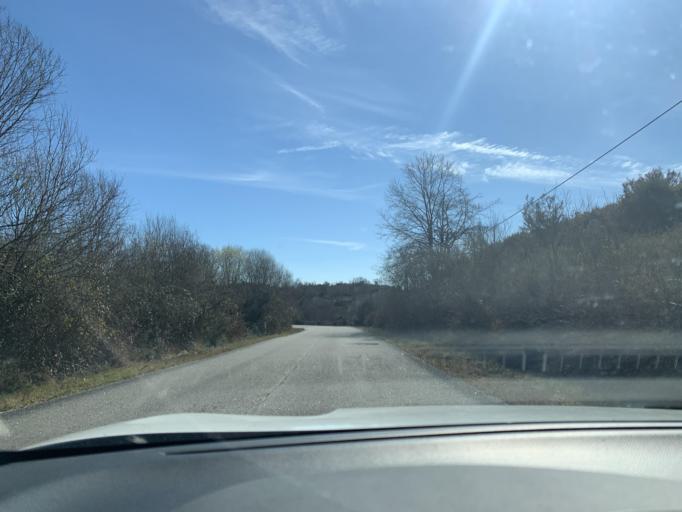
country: PT
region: Viseu
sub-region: Concelho de Tondela
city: Tondela
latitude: 40.6005
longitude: -8.0273
